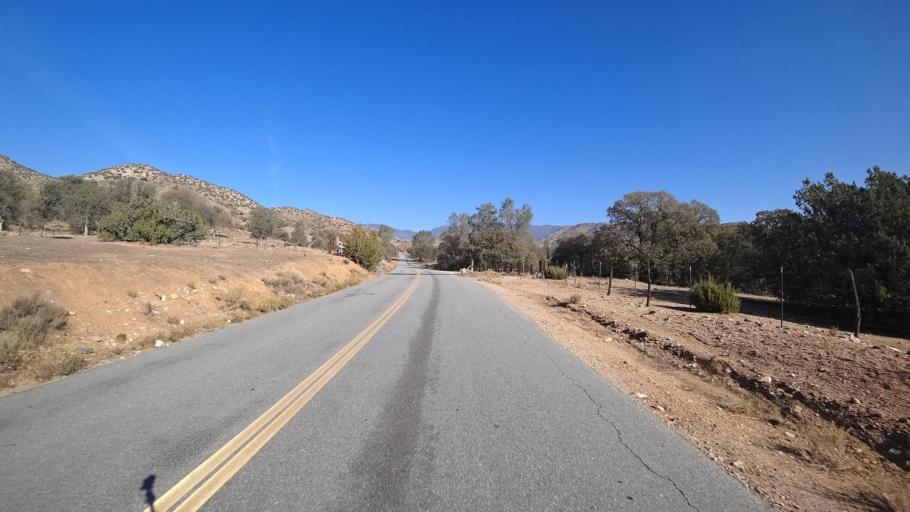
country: US
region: California
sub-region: Kern County
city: Tehachapi
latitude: 35.3415
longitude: -118.3867
